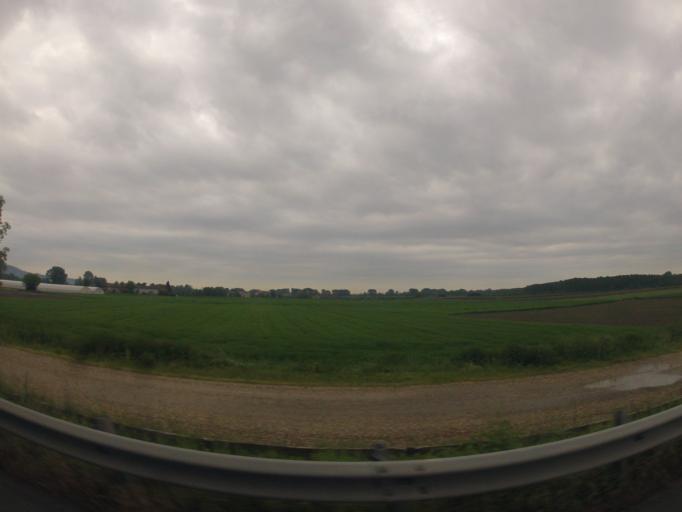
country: IT
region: Piedmont
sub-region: Provincia di Torino
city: La Loggia
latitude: 44.9576
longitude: 7.6810
